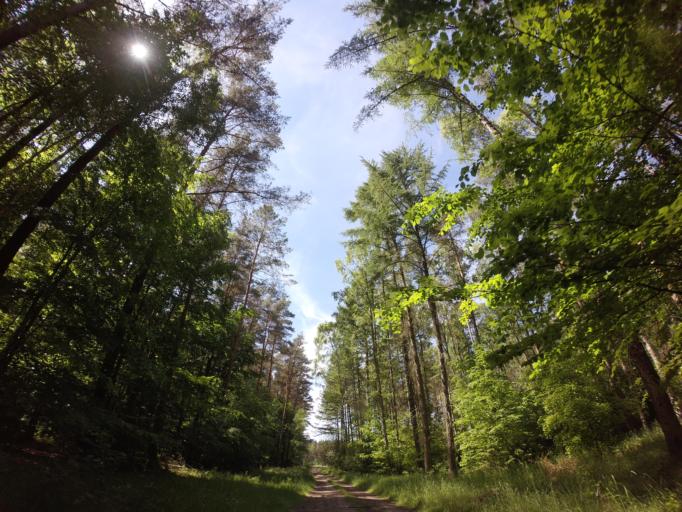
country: PL
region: West Pomeranian Voivodeship
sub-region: Powiat drawski
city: Kalisz Pomorski
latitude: 53.1644
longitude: 15.8963
